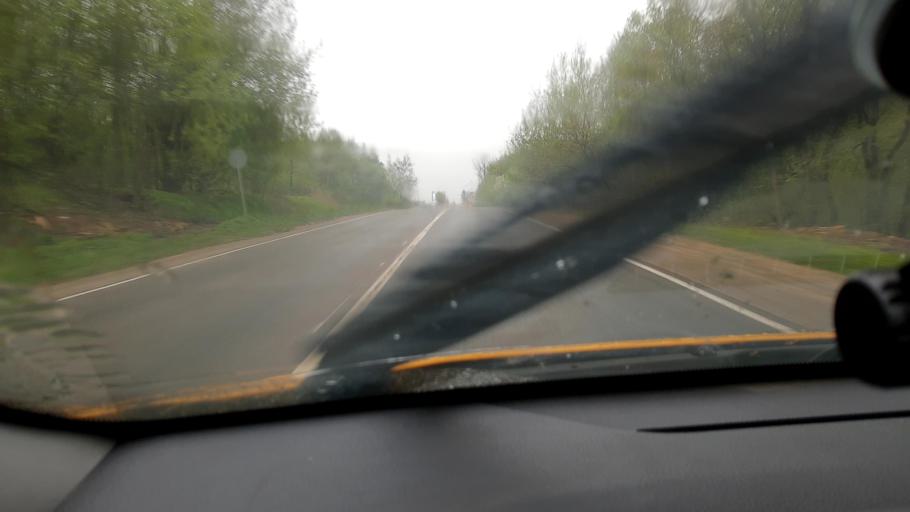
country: RU
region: Tula
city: Zaokskiy
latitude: 54.7523
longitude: 37.4384
